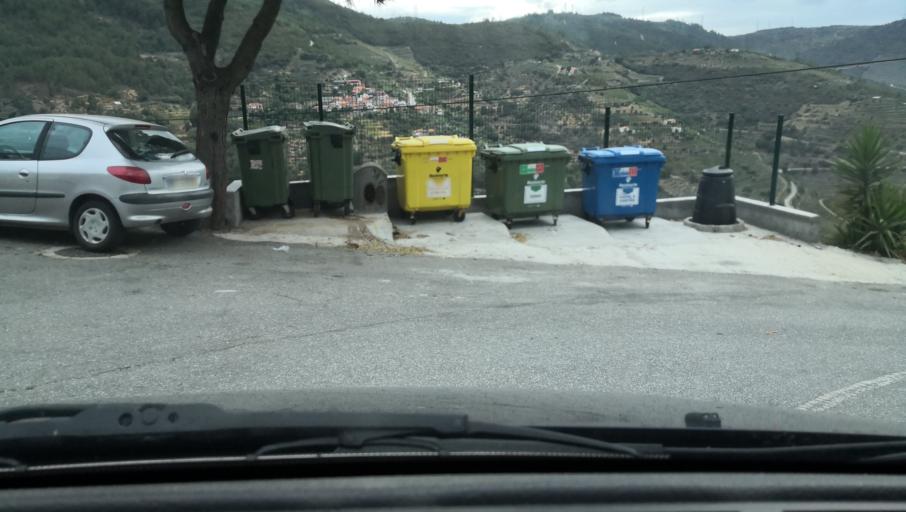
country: PT
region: Viseu
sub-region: Tabuaco
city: Tabuaco
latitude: 41.1266
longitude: -7.6269
